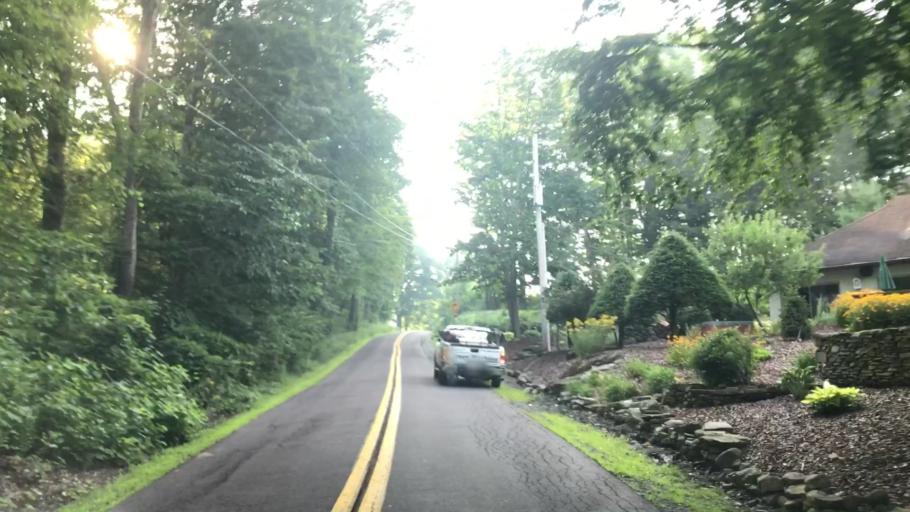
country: US
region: Pennsylvania
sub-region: Wyoming County
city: Factoryville
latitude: 41.6169
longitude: -75.7484
